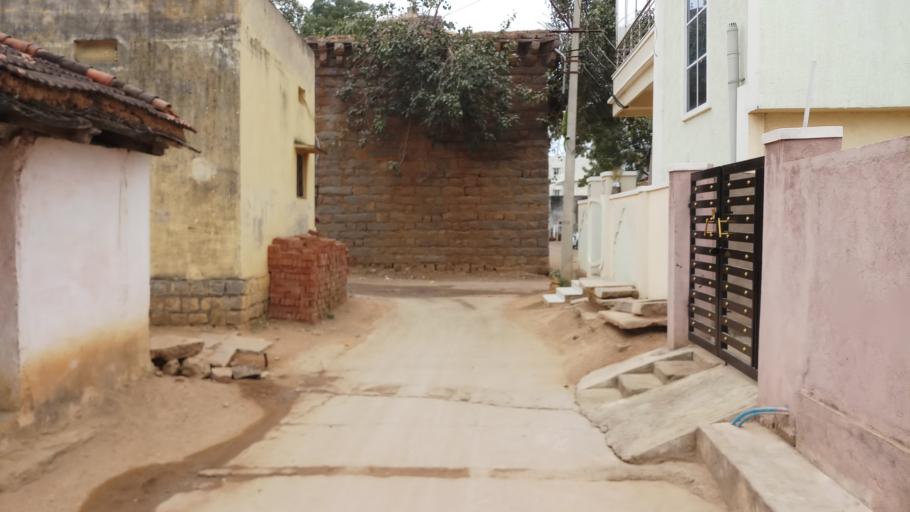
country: IN
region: Telangana
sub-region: Rangareddi
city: Quthbullapur
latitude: 17.6668
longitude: 78.4696
